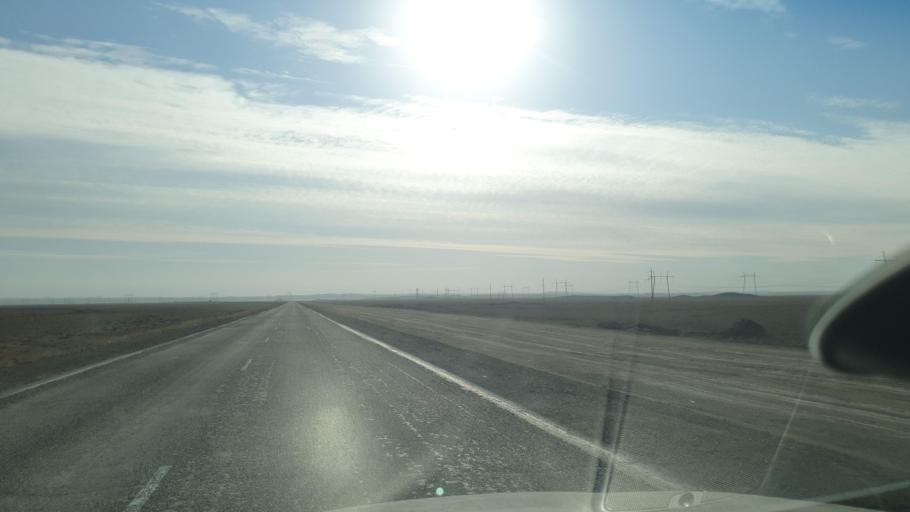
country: KZ
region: Zhambyl
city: Mynaral
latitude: 45.6240
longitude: 73.3964
